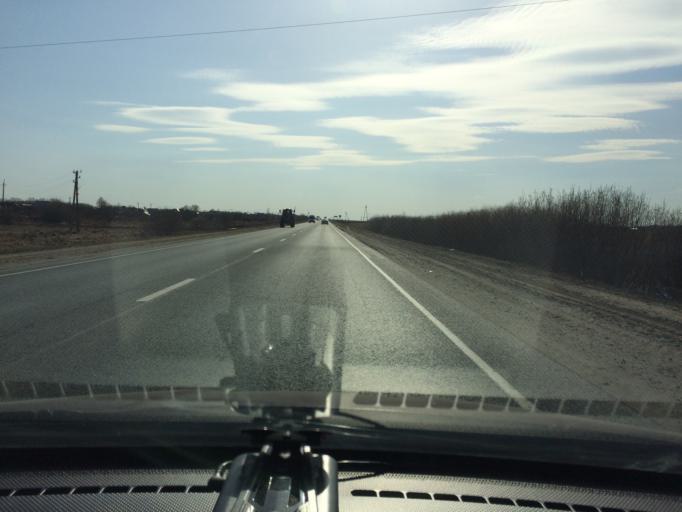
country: RU
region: Mariy-El
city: Yoshkar-Ola
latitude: 56.6730
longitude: 48.0076
